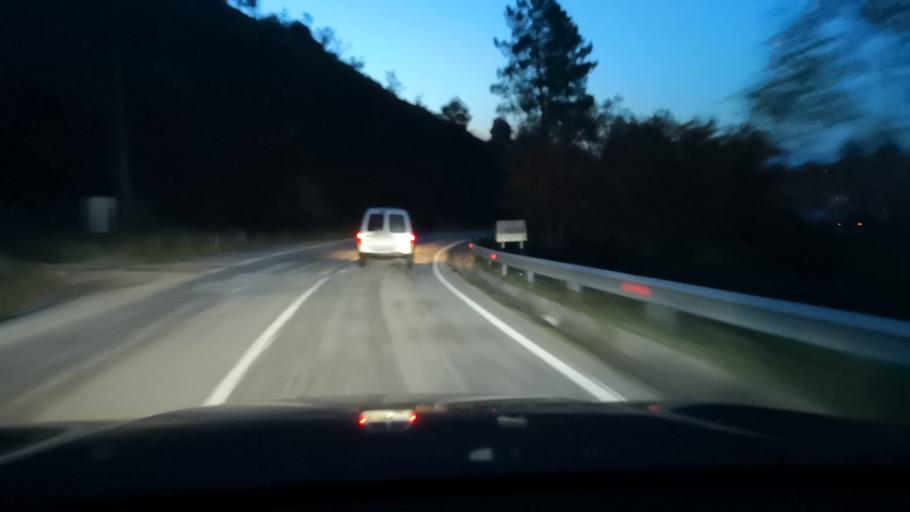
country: PT
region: Porto
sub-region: Baiao
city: Baiao
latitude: 41.2326
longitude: -8.0143
